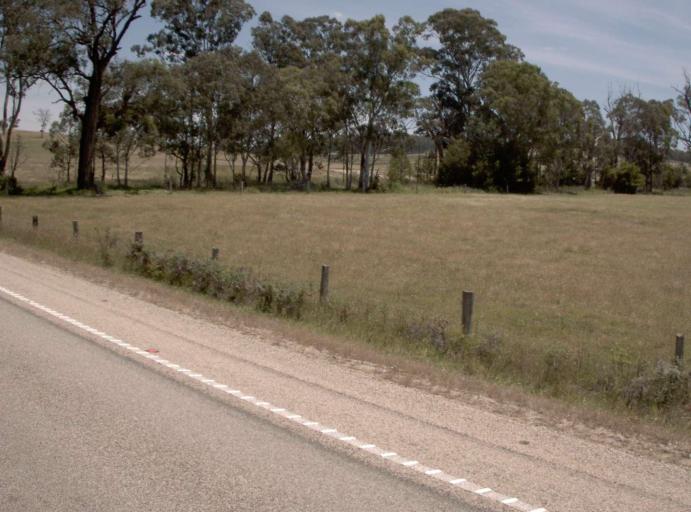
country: AU
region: Victoria
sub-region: East Gippsland
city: Bairnsdale
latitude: -37.7631
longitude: 147.7007
